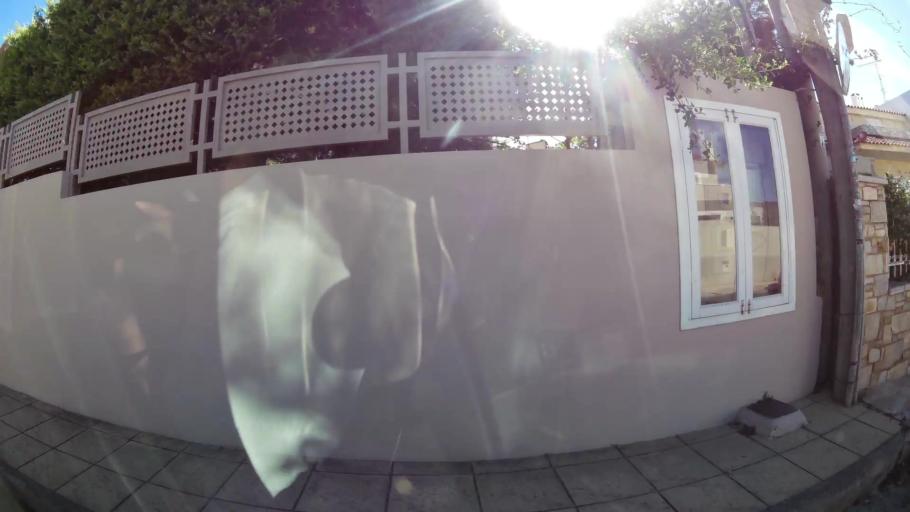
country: GR
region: Attica
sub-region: Nomarchia Anatolikis Attikis
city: Vari
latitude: 37.8338
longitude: 23.8217
